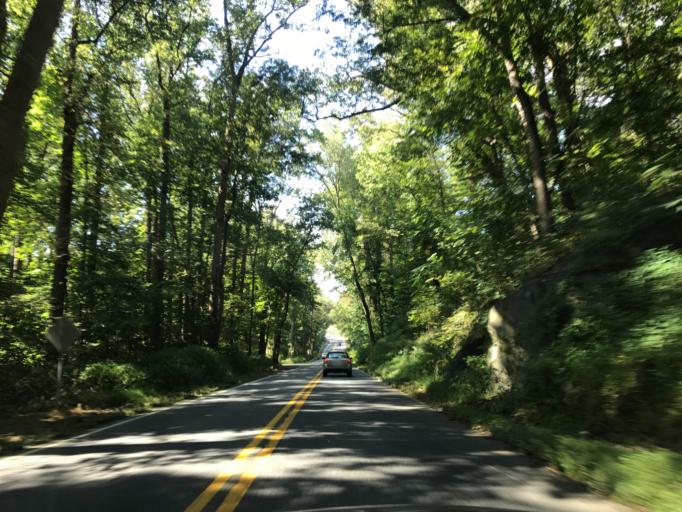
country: US
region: Maryland
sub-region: Cecil County
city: Rising Sun
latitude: 39.6652
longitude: -76.1653
